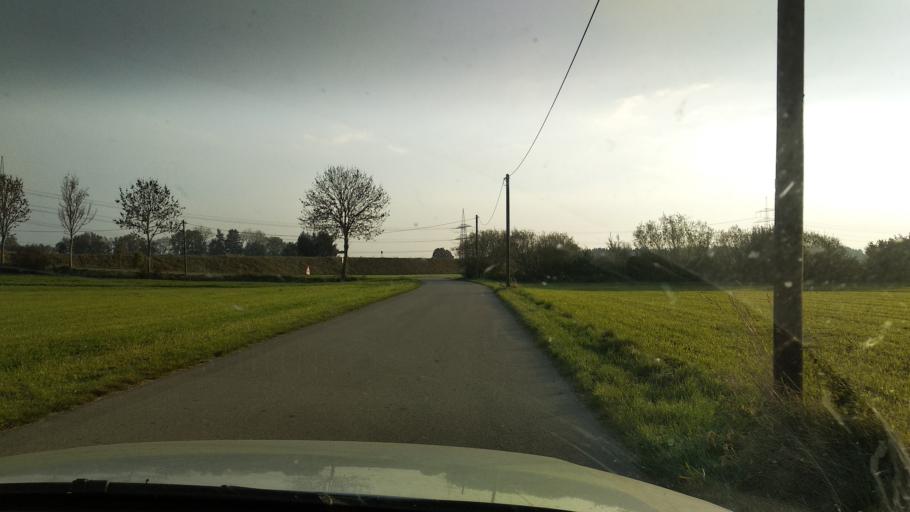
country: DE
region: Bavaria
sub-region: Upper Bavaria
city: Ottenhofen
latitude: 48.2142
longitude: 11.8925
